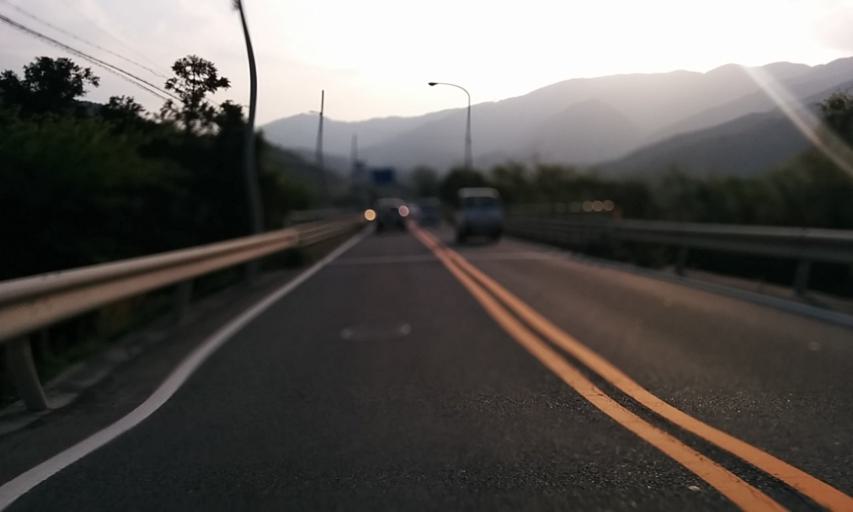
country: JP
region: Ehime
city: Saijo
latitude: 33.8576
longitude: 133.0239
